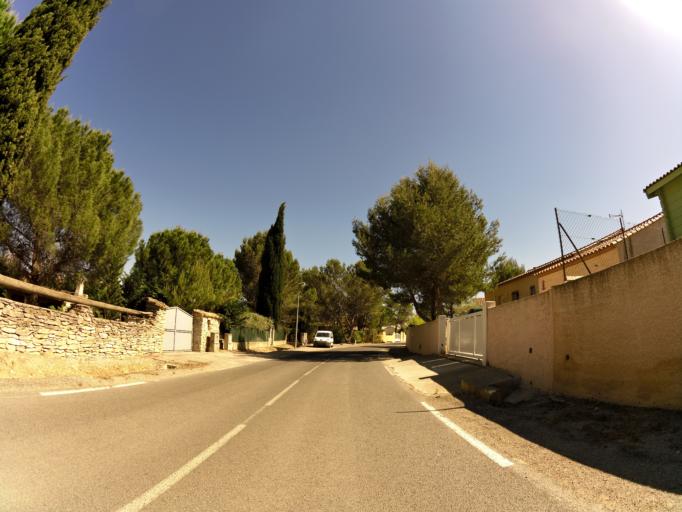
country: FR
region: Languedoc-Roussillon
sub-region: Departement de l'Herault
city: Villetelle
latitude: 43.7327
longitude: 4.1345
